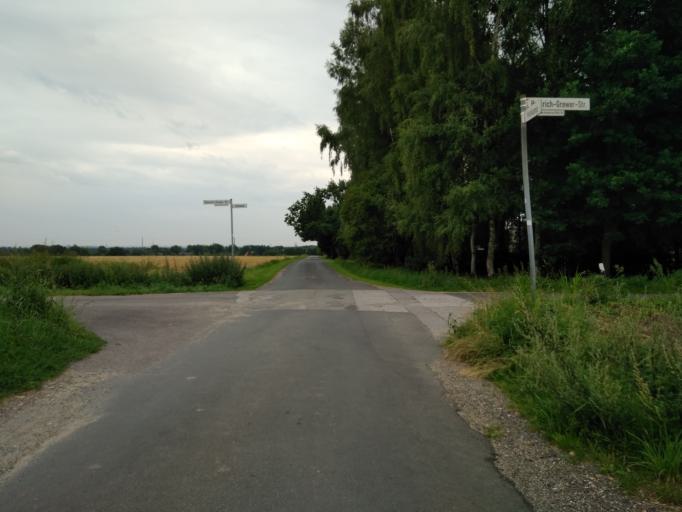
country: DE
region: North Rhine-Westphalia
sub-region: Regierungsbezirk Munster
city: Bottrop
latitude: 51.6010
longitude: 6.9008
